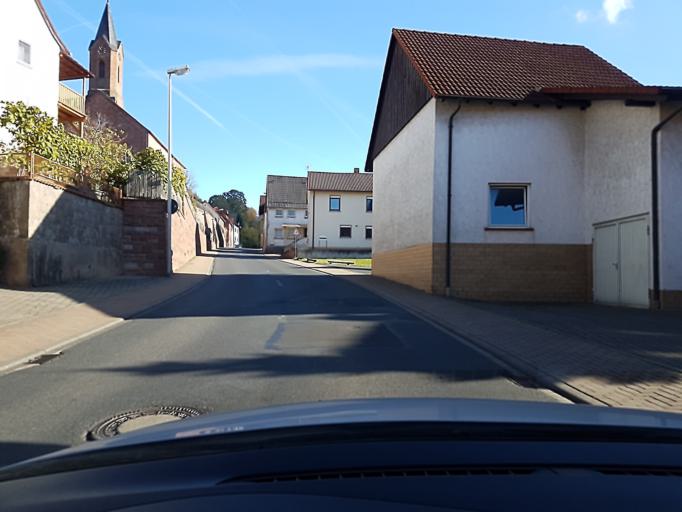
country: DE
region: Bavaria
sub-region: Regierungsbezirk Unterfranken
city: Hausen
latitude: 49.8705
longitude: 9.2133
